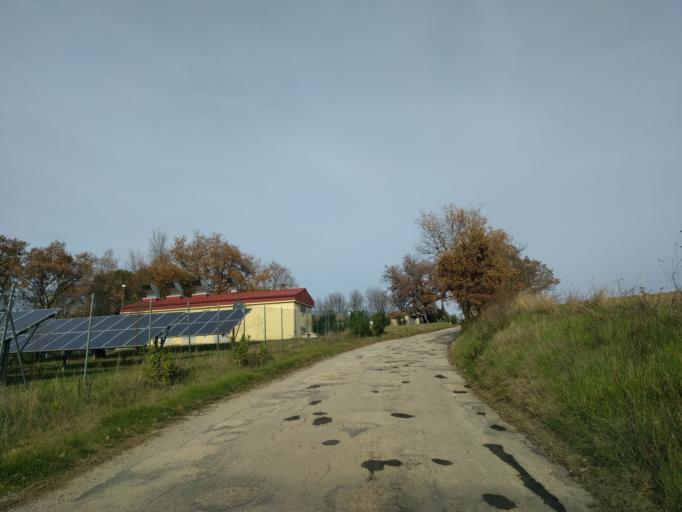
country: IT
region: The Marches
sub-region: Provincia di Pesaro e Urbino
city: Cuccurano
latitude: 43.8035
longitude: 12.9417
